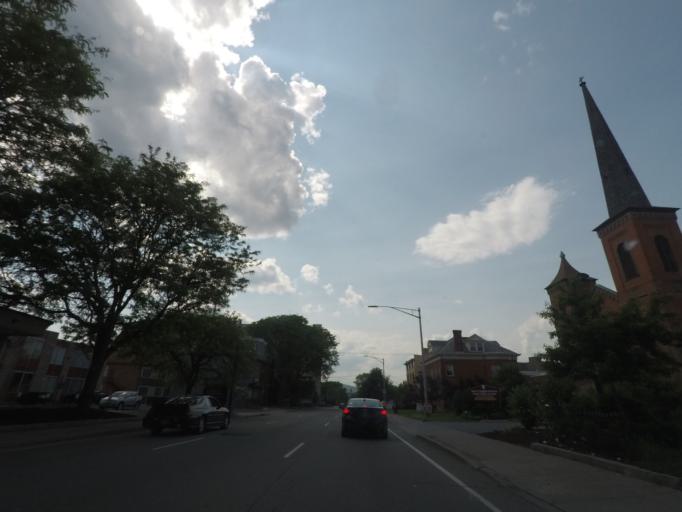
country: US
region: New York
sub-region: Dutchess County
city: Poughkeepsie
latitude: 41.7052
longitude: -73.9268
